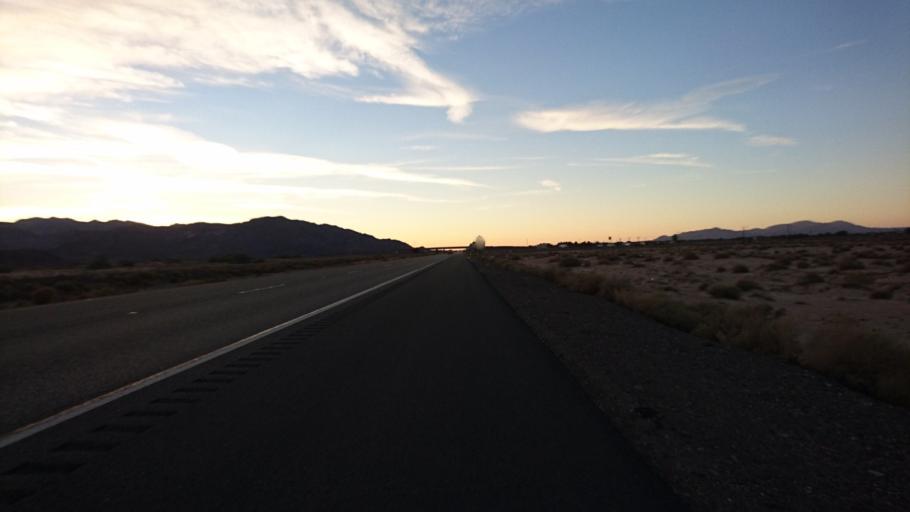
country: US
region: California
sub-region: San Bernardino County
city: Barstow
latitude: 34.8151
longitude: -116.6017
